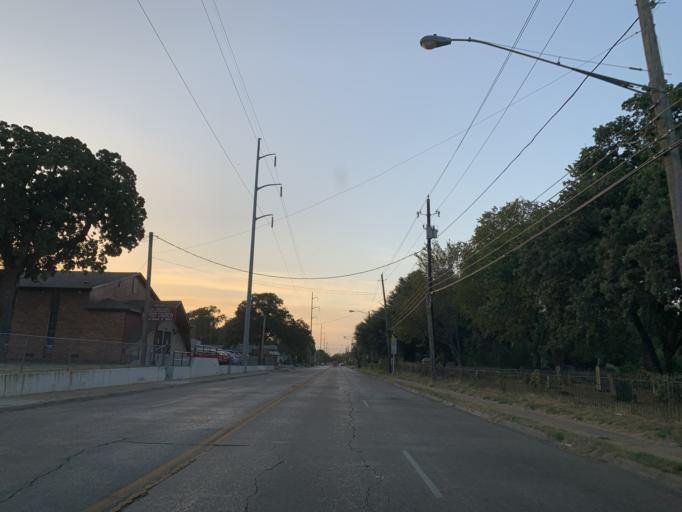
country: US
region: Texas
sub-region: Dallas County
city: Dallas
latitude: 32.7617
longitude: -96.7597
